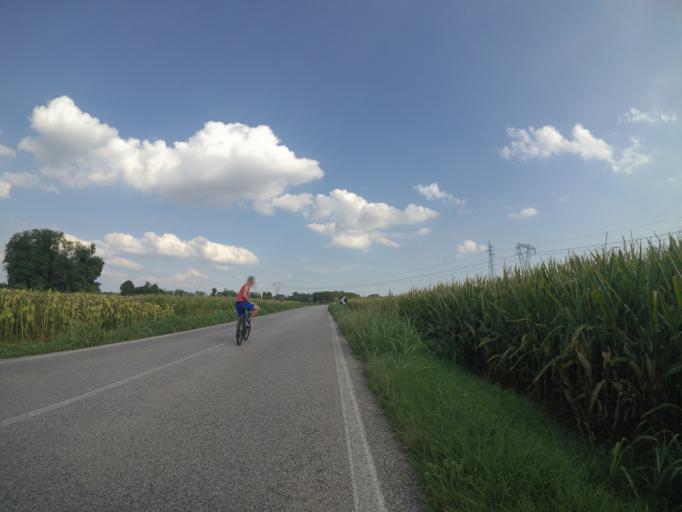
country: IT
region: Friuli Venezia Giulia
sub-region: Provincia di Udine
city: Basiliano-Vissandone
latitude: 46.0493
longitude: 13.0905
